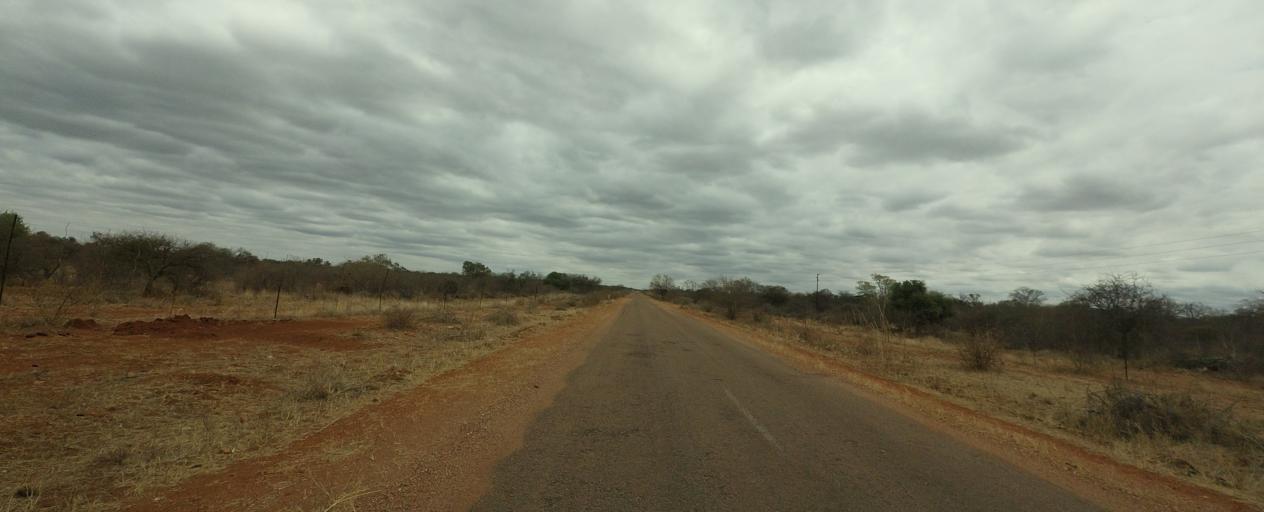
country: BW
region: Central
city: Mathathane
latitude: -22.7394
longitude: 28.4719
